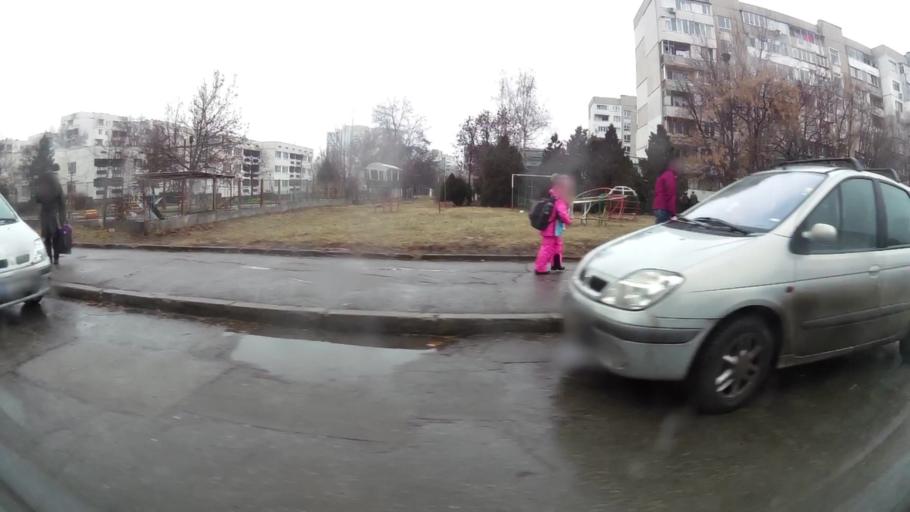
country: BG
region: Sofia-Capital
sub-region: Stolichna Obshtina
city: Sofia
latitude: 42.6384
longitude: 23.3763
